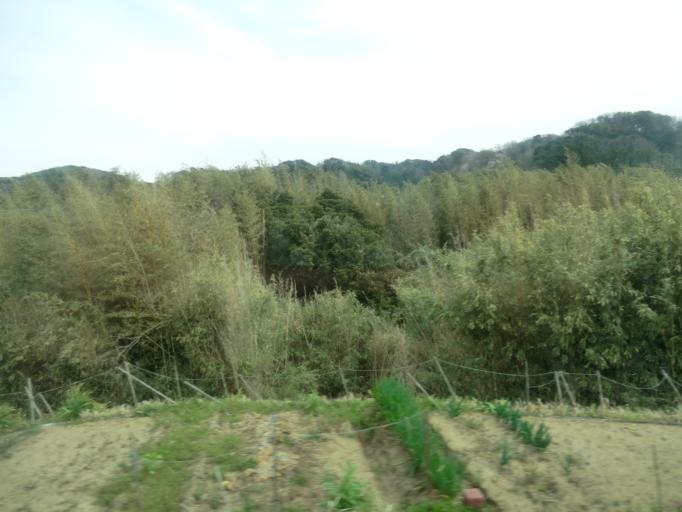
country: JP
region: Chiba
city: Futtsu
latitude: 35.2732
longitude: 139.8637
